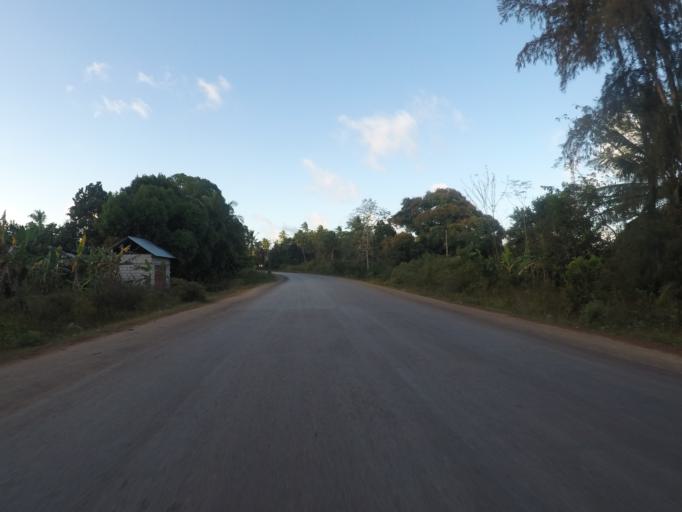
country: TZ
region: Zanzibar Central/South
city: Koani
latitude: -6.1802
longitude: 39.3281
